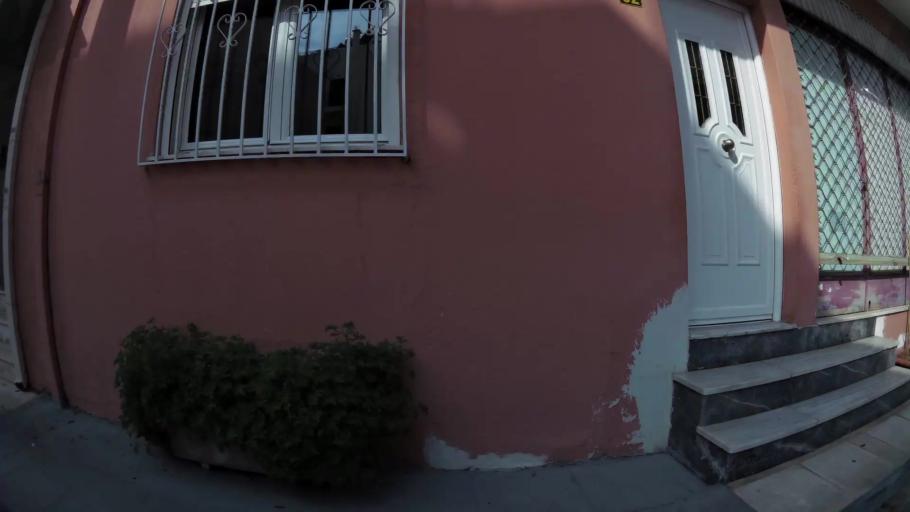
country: GR
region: Attica
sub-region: Nomarchia Athinas
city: Chaidari
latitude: 38.0171
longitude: 23.6779
